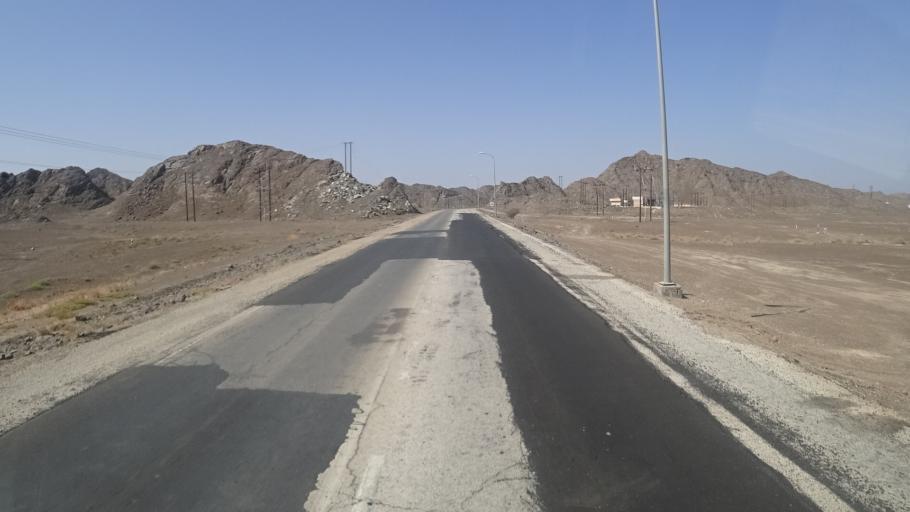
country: OM
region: Ash Sharqiyah
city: Ibra'
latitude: 22.6851
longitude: 58.5719
